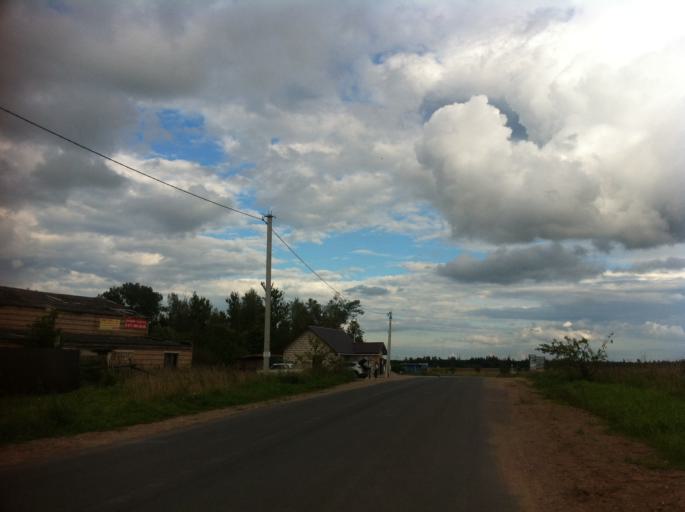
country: RU
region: Pskov
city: Izborsk
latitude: 57.8380
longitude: 27.9856
